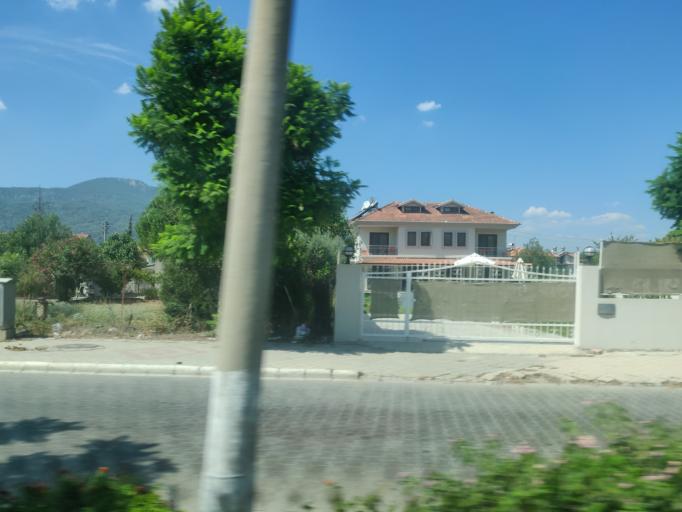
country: TR
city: Dalyan
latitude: 36.8402
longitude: 28.6510
